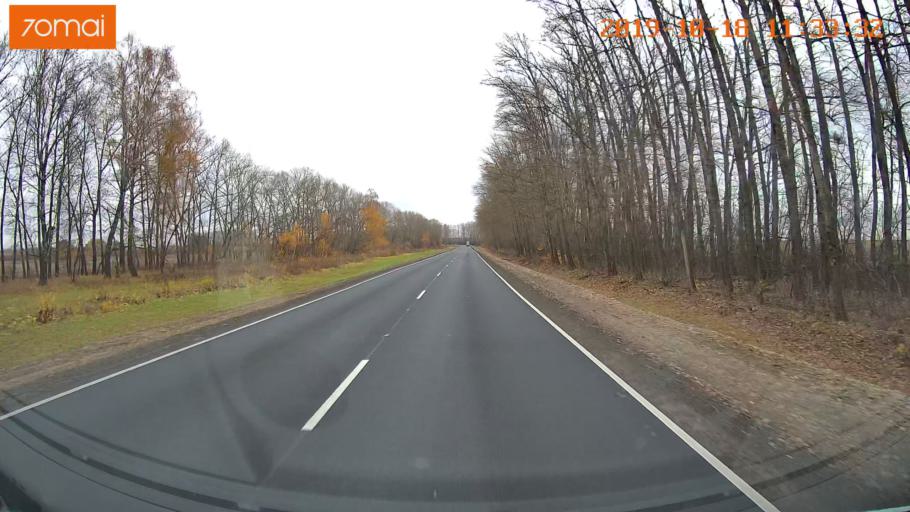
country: RU
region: Rjazan
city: Oktyabr'skiy
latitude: 54.1405
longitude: 38.7426
